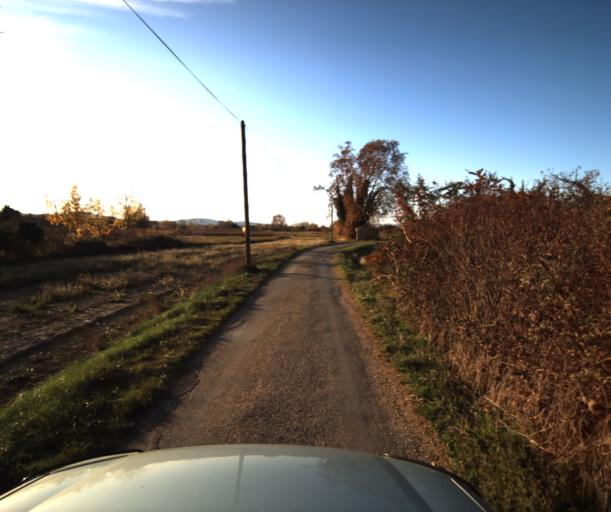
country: FR
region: Provence-Alpes-Cote d'Azur
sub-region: Departement des Bouches-du-Rhone
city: Meyrargues
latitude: 43.6675
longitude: 5.5355
